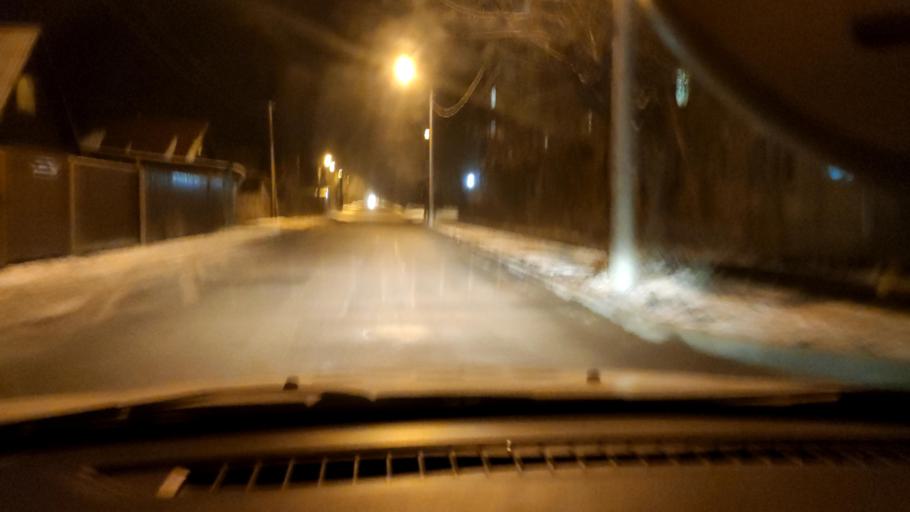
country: RU
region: Perm
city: Overyata
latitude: 58.0298
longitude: 55.8423
